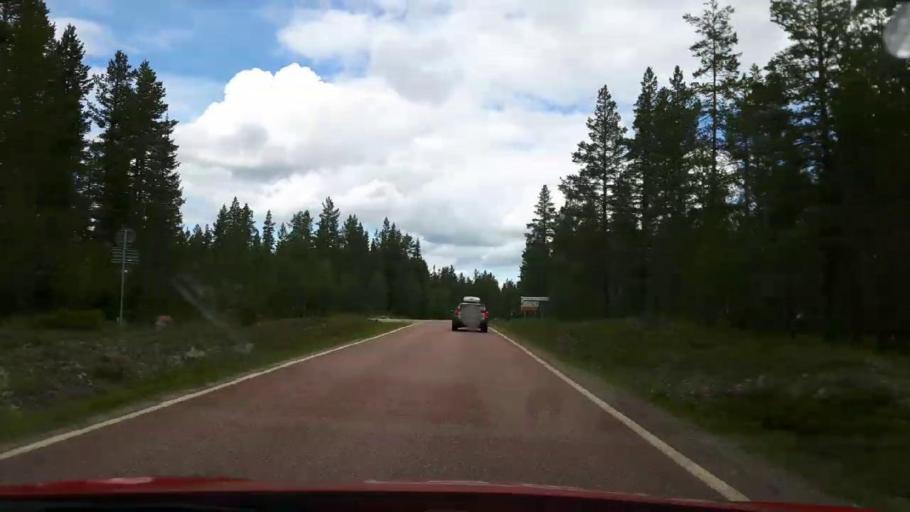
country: NO
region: Hedmark
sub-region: Trysil
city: Innbygda
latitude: 61.8636
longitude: 12.9523
